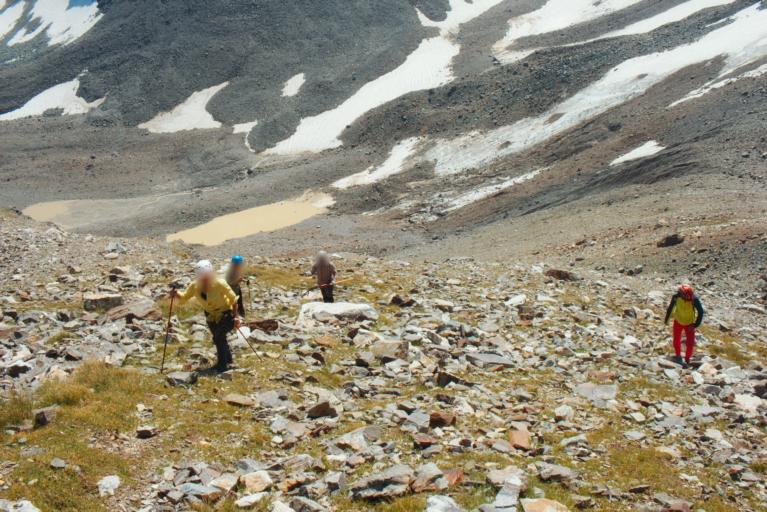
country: RU
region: Karachayevo-Cherkesiya
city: Nizhniy Arkhyz
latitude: 43.4267
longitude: 41.2439
